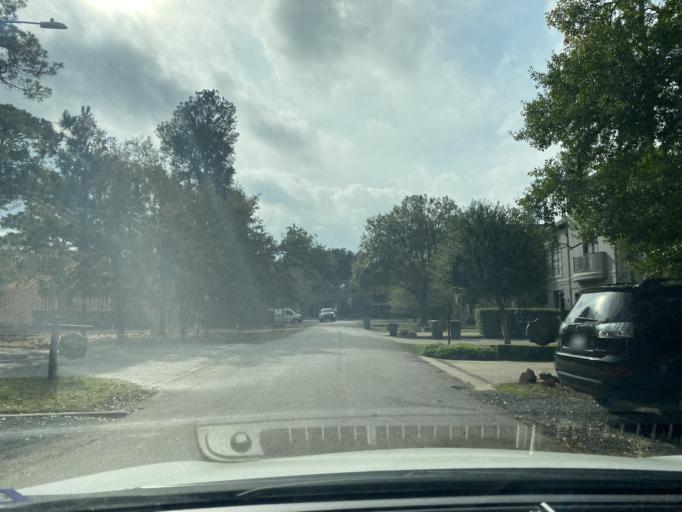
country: US
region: Texas
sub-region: Harris County
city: Hunters Creek Village
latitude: 29.7668
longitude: -95.4734
